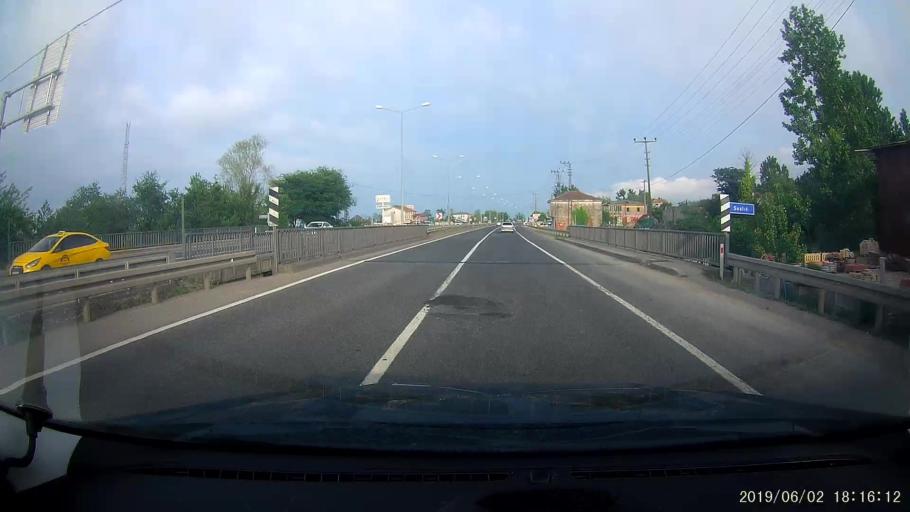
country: TR
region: Ordu
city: Unieh
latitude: 41.1026
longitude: 37.3941
